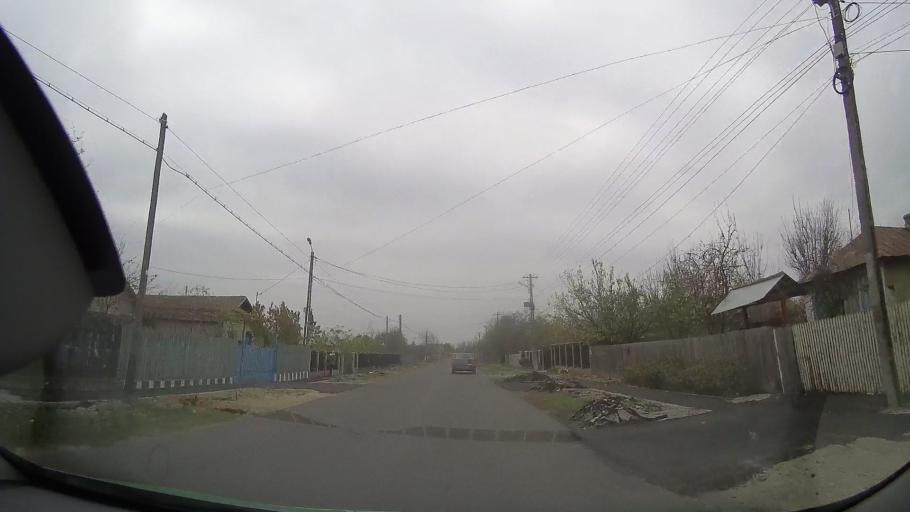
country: RO
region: Buzau
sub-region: Comuna Pogoanele
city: Pogoanele
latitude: 44.9224
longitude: 26.9938
